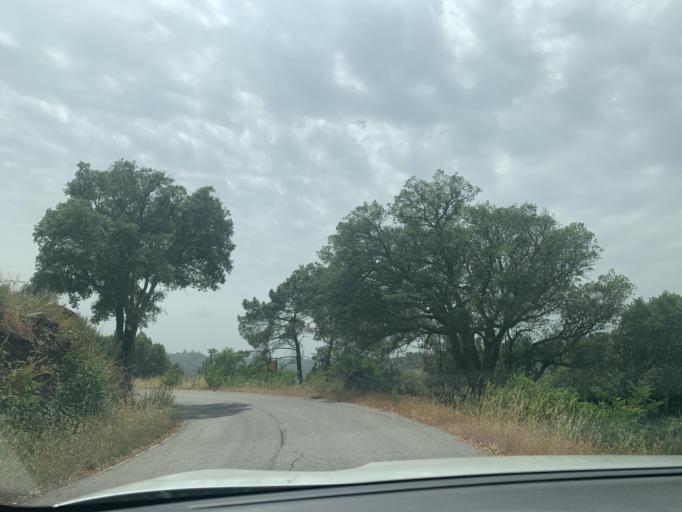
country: PT
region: Guarda
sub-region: Fornos de Algodres
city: Fornos de Algodres
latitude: 40.5694
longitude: -7.5979
